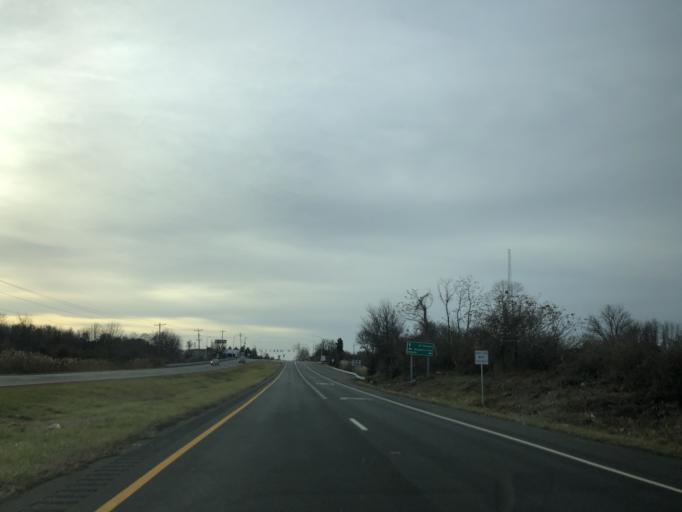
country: US
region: Delaware
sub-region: New Castle County
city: Bear
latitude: 39.5824
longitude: -75.6584
